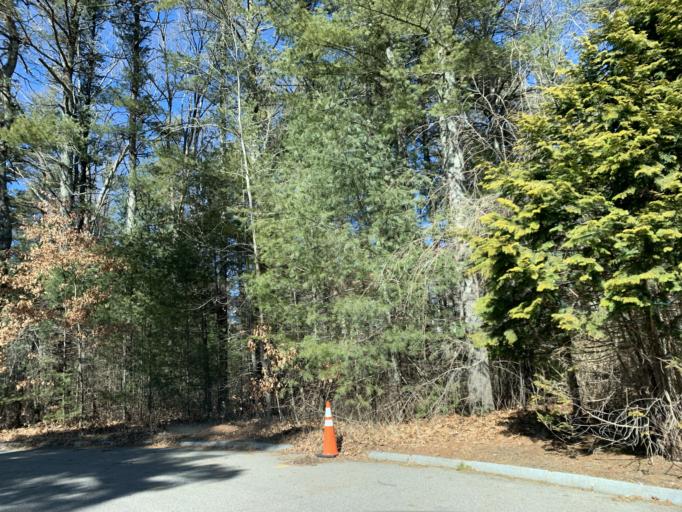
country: US
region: Massachusetts
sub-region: Bristol County
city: Norton
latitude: 41.9468
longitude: -71.1635
